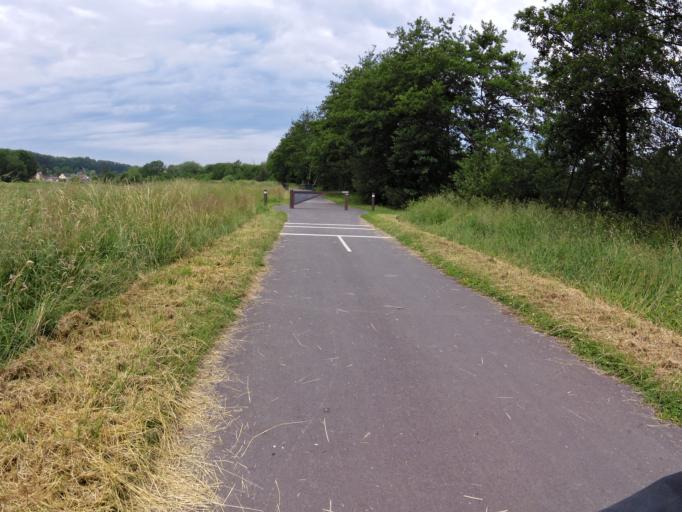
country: FR
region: Champagne-Ardenne
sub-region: Departement des Ardennes
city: Donchery
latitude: 49.6929
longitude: 4.8826
